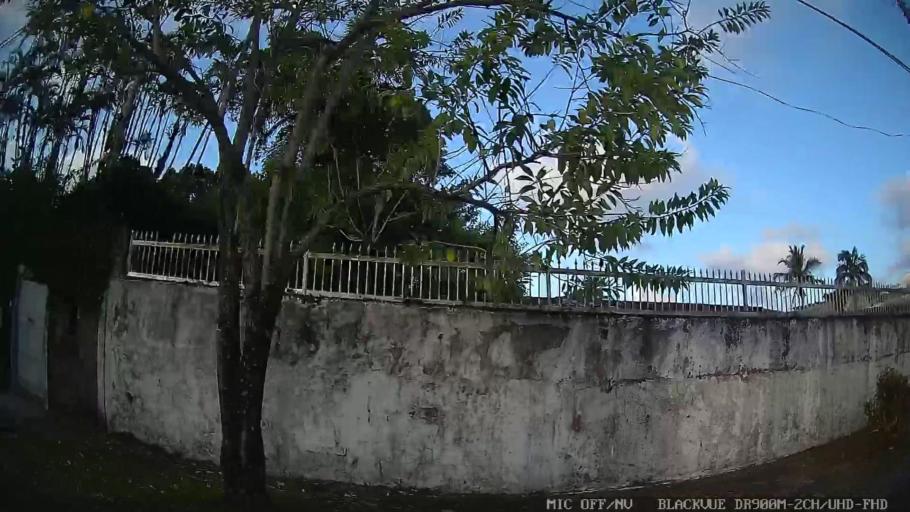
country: BR
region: Sao Paulo
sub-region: Peruibe
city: Peruibe
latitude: -24.3173
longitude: -46.9989
